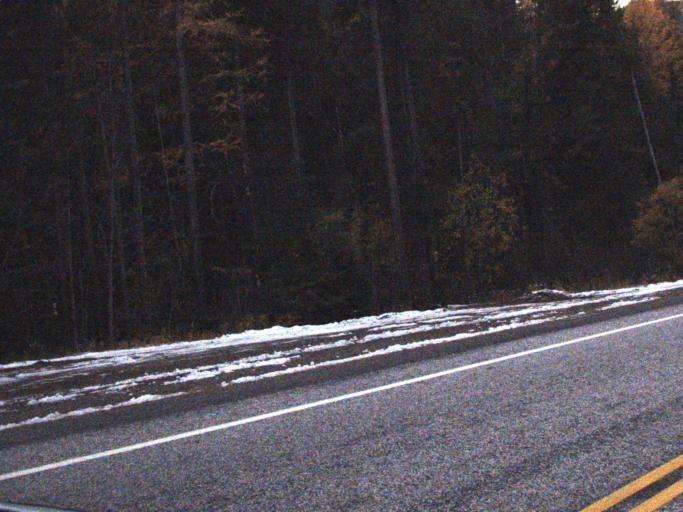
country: US
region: Washington
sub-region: Ferry County
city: Republic
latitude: 48.6220
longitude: -118.4333
